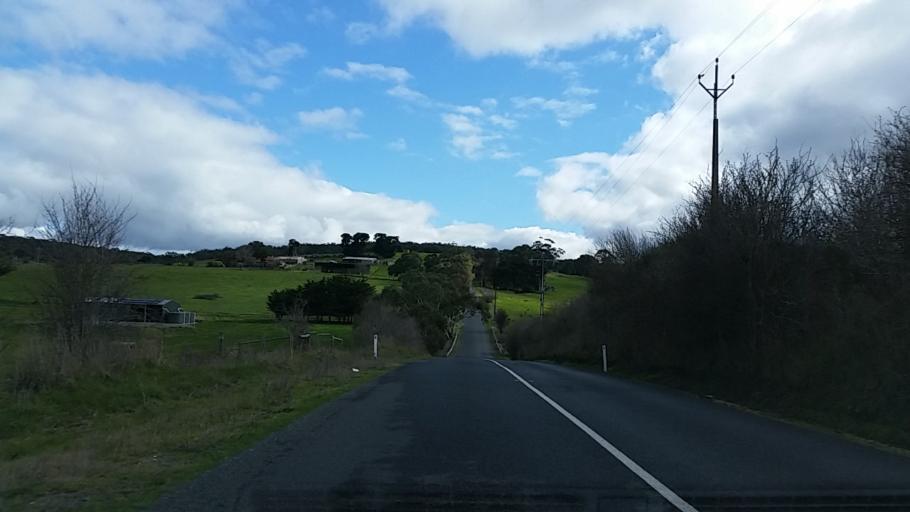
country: AU
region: South Australia
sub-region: Mount Barker
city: Little Hampton
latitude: -35.0749
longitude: 138.8386
